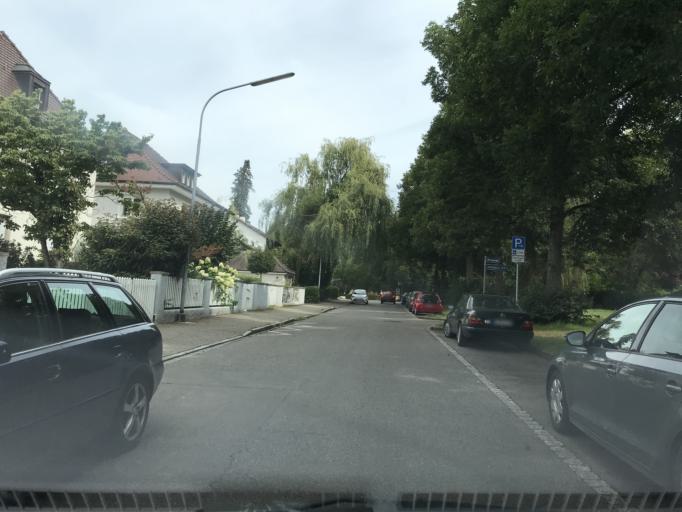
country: DE
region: Baden-Wuerttemberg
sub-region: Freiburg Region
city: Loerrach
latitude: 47.6052
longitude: 7.6654
